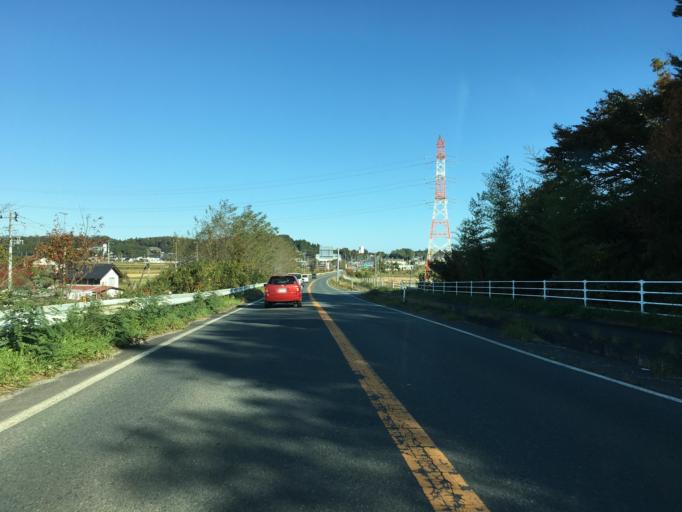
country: JP
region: Miyagi
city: Marumori
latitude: 37.8491
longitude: 140.9165
